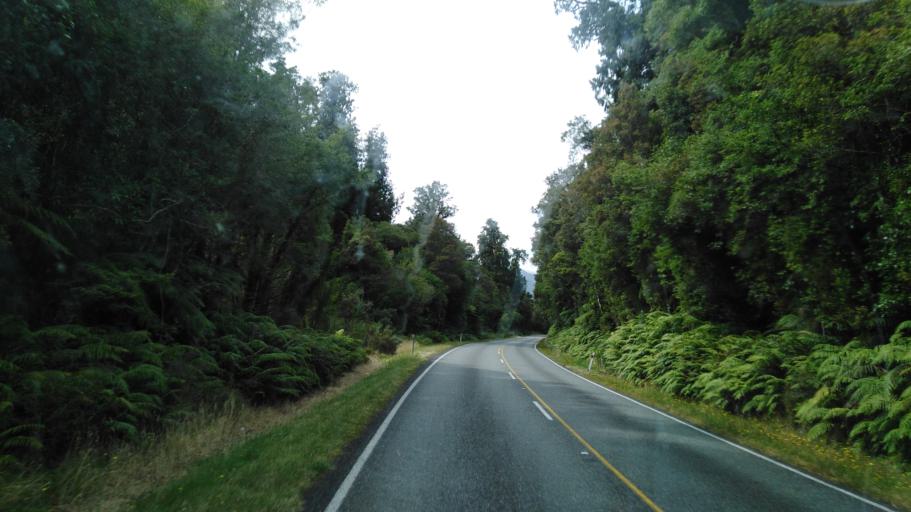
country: NZ
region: West Coast
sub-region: Grey District
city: Greymouth
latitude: -42.6952
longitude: 171.2295
